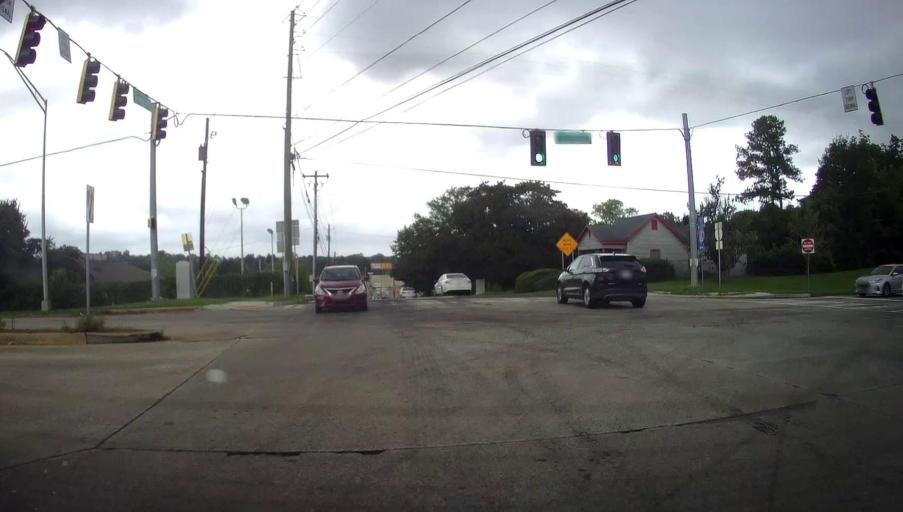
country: US
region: Georgia
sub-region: Bibb County
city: Macon
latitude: 32.8482
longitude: -83.6209
